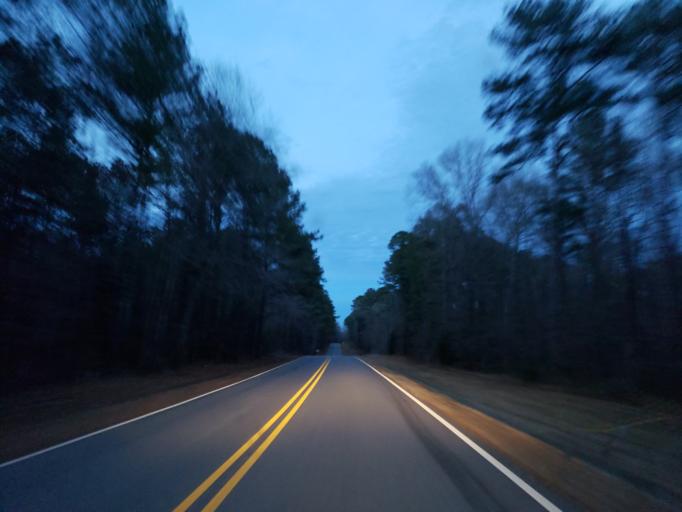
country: US
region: Alabama
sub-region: Greene County
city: Eutaw
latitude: 32.8975
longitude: -88.0307
